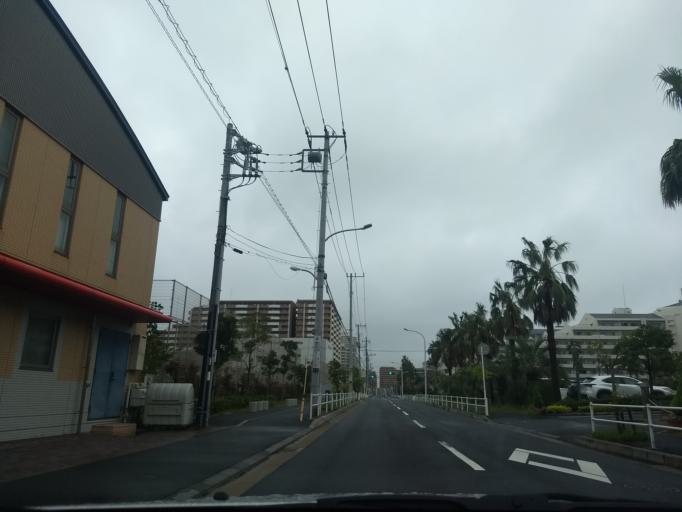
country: JP
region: Tokyo
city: Urayasu
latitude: 35.6346
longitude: 139.9170
